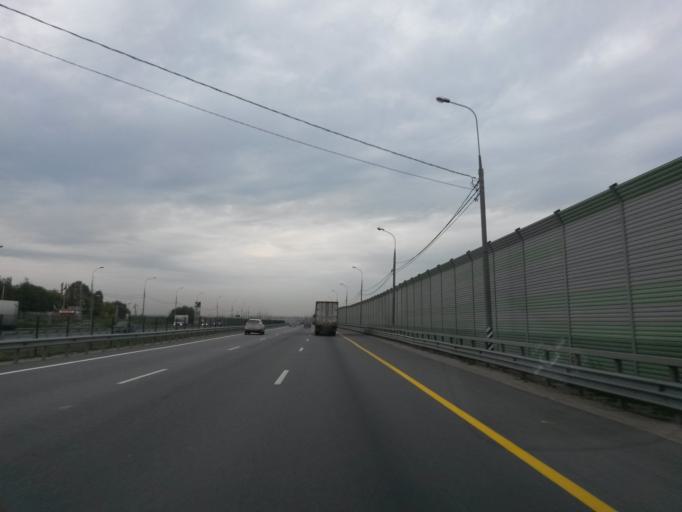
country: RU
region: Moskovskaya
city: Yam
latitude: 55.4763
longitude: 37.7487
